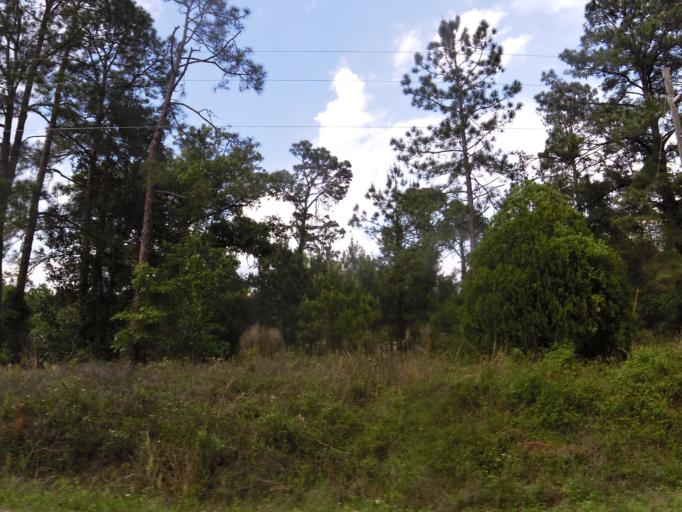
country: US
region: Georgia
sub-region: Charlton County
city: Folkston
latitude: 30.8048
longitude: -82.0345
